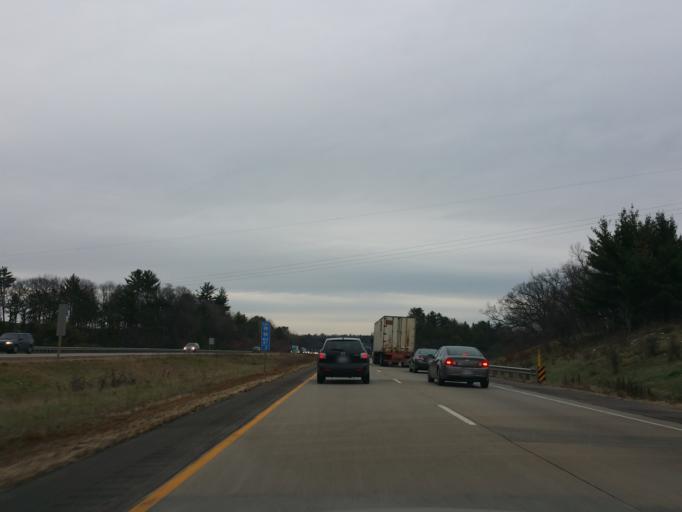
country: US
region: Wisconsin
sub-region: Sauk County
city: Lake Delton
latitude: 43.6346
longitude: -89.8088
